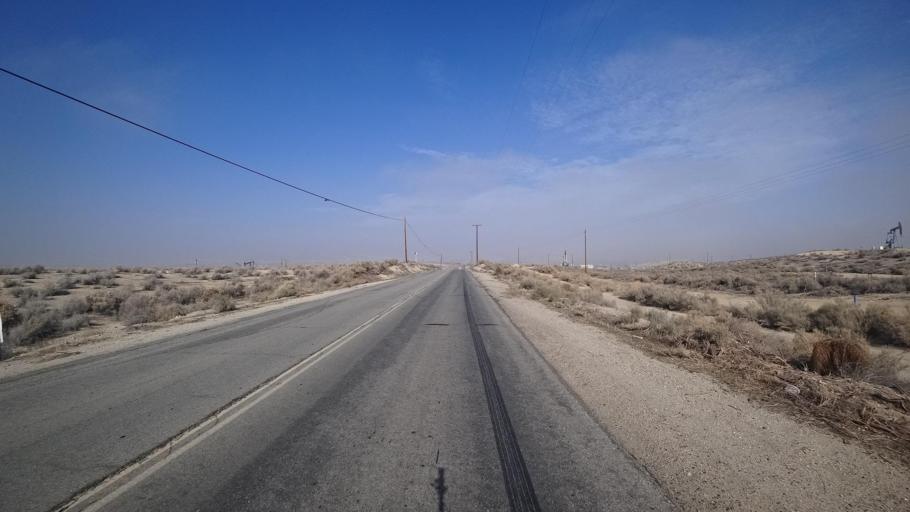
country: US
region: California
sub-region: Kern County
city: Ford City
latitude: 35.1714
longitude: -119.4653
